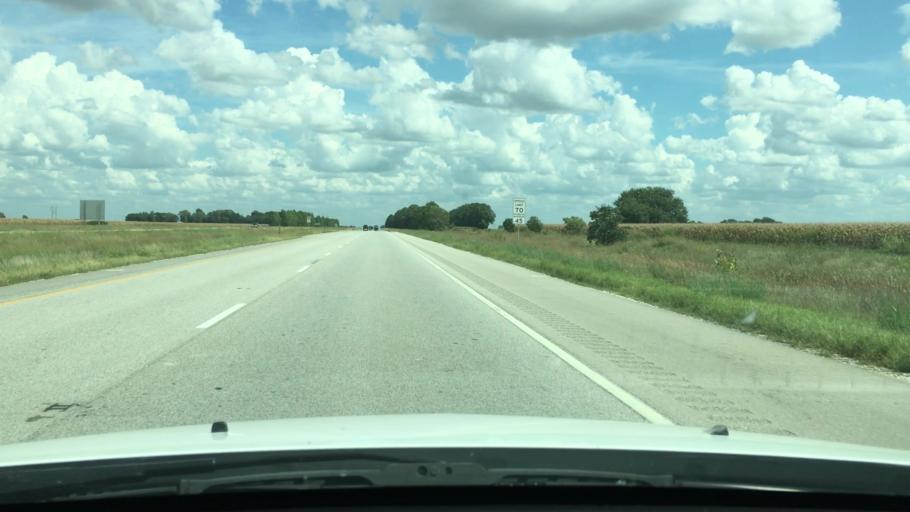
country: US
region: Illinois
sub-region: Sangamon County
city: New Berlin
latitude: 39.7368
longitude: -90.0299
